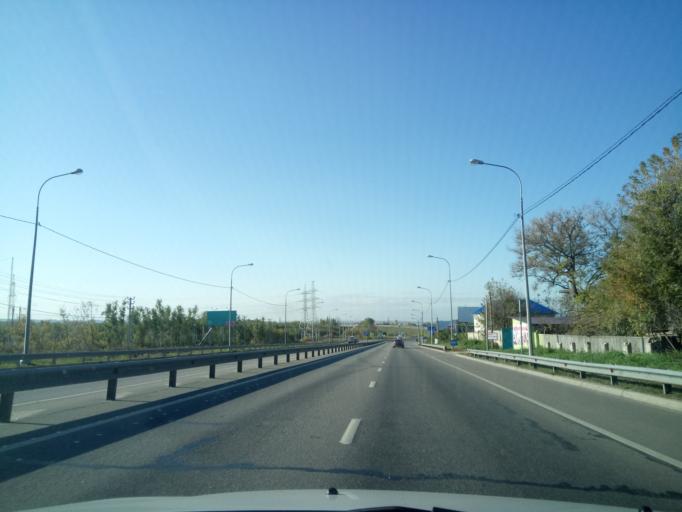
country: RU
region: Nizjnij Novgorod
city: Burevestnik
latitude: 56.1847
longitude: 43.9206
